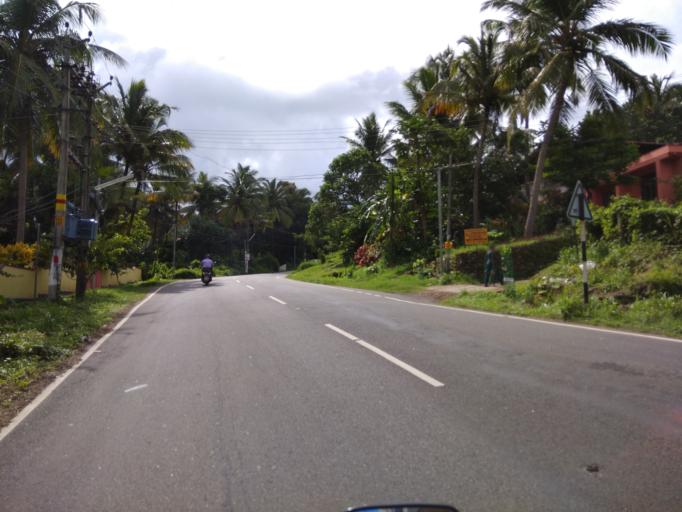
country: IN
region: Kerala
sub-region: Thrissur District
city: Trichur
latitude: 10.5351
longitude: 76.3371
